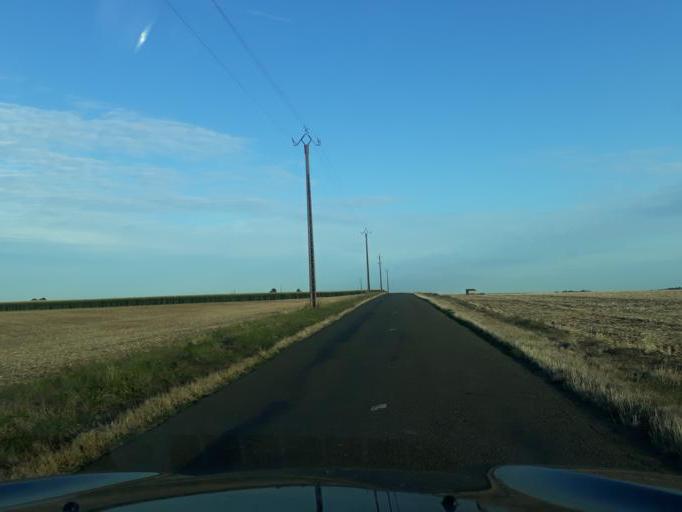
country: FR
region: Centre
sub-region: Departement du Loiret
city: Epieds-en-Beauce
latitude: 47.9456
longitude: 1.5702
